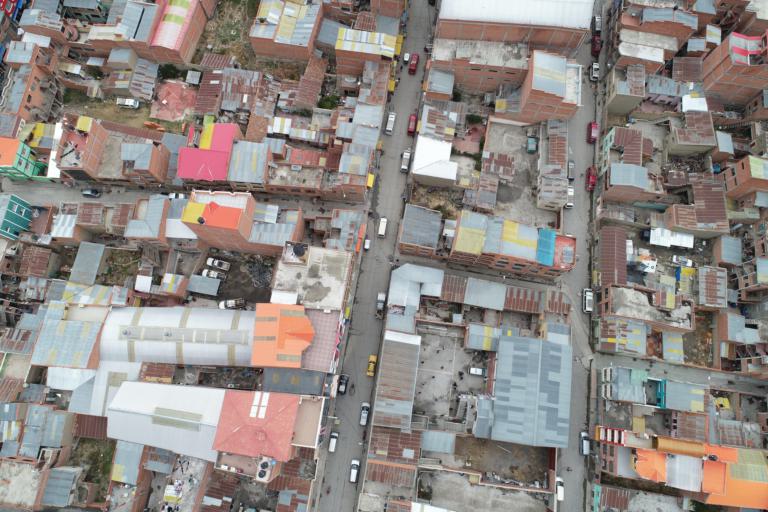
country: BO
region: La Paz
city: Achacachi
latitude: -16.0455
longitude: -68.6839
